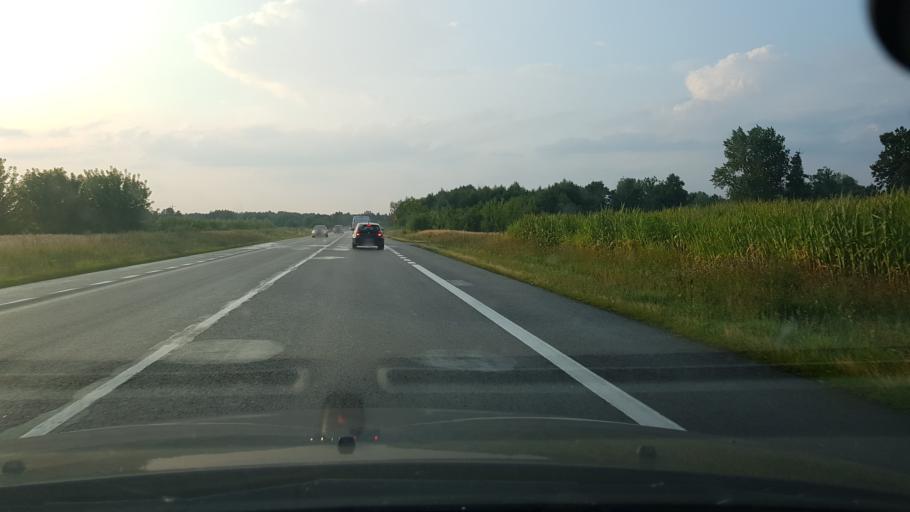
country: PL
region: Masovian Voivodeship
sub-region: Powiat ciechanowski
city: Glinojeck
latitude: 52.7960
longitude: 20.2713
